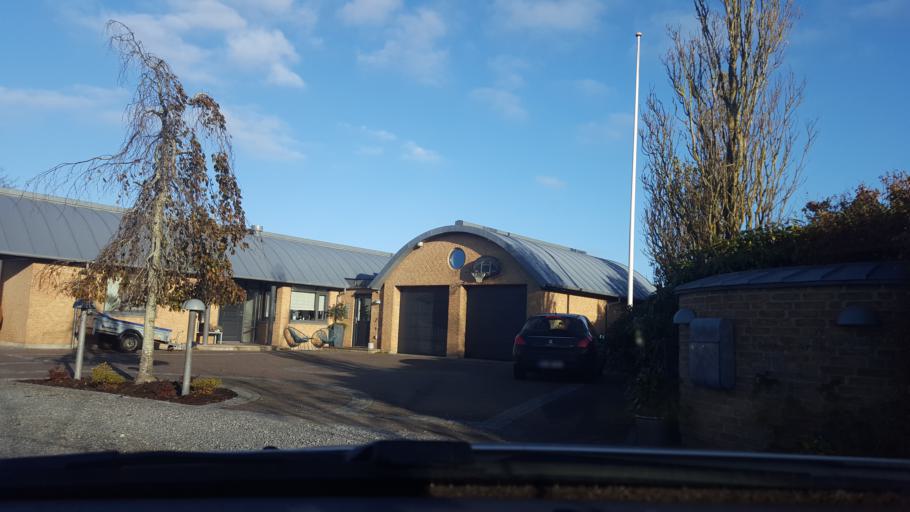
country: DK
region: North Denmark
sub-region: Morso Kommune
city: Nykobing Mors
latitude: 56.7544
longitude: 8.8742
